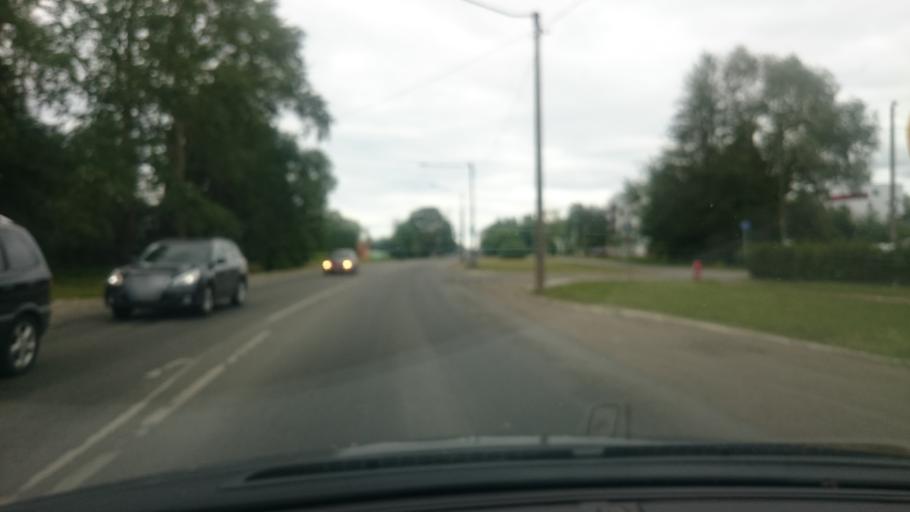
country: EE
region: Harju
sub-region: Saue vald
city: Laagri
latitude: 59.4143
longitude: 24.6343
